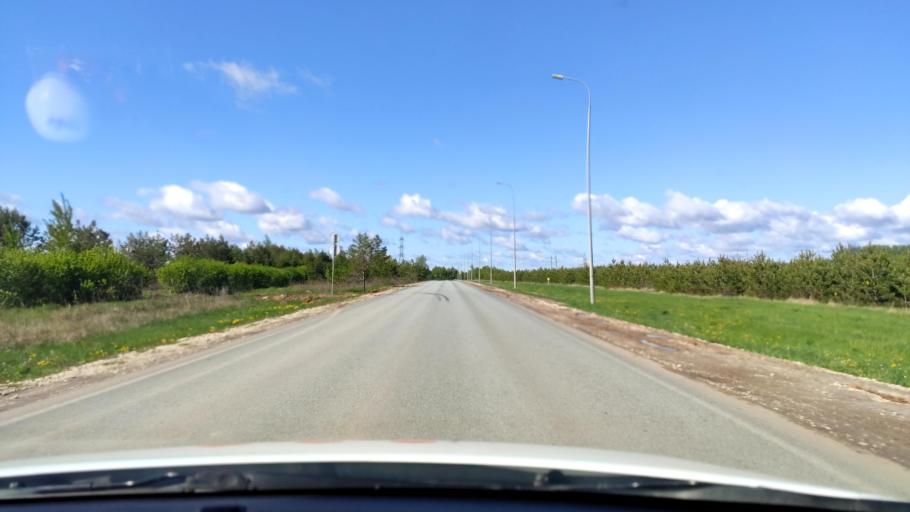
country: RU
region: Tatarstan
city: Sviyazhsk
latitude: 55.7269
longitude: 48.7561
